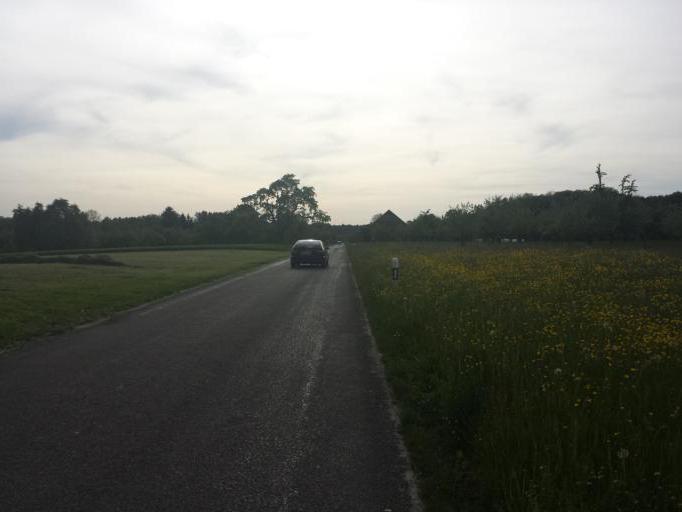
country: CH
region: Thurgau
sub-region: Arbon District
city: Salmsach
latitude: 47.5443
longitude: 9.3436
